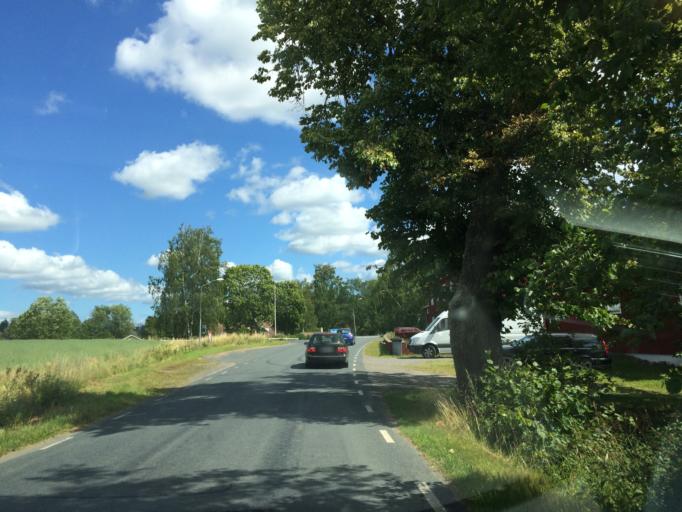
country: SE
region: Soedermanland
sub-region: Katrineholms Kommun
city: Katrineholm
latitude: 59.0671
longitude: 16.3570
